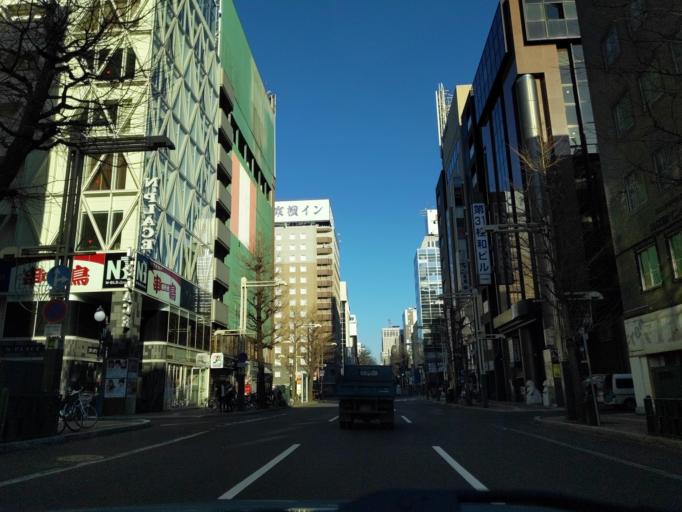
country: JP
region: Hokkaido
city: Sapporo
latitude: 43.0549
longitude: 141.3550
